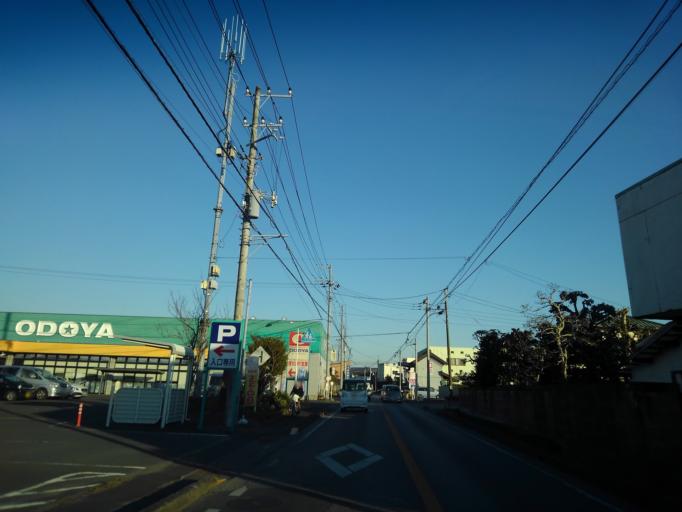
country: JP
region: Chiba
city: Kimitsu
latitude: 35.3057
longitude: 139.9569
